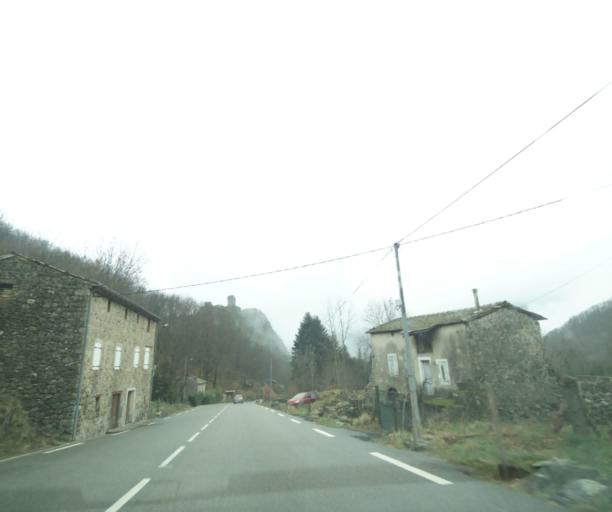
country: FR
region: Rhone-Alpes
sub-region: Departement de l'Ardeche
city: Thueyts
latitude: 44.6760
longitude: 4.0980
